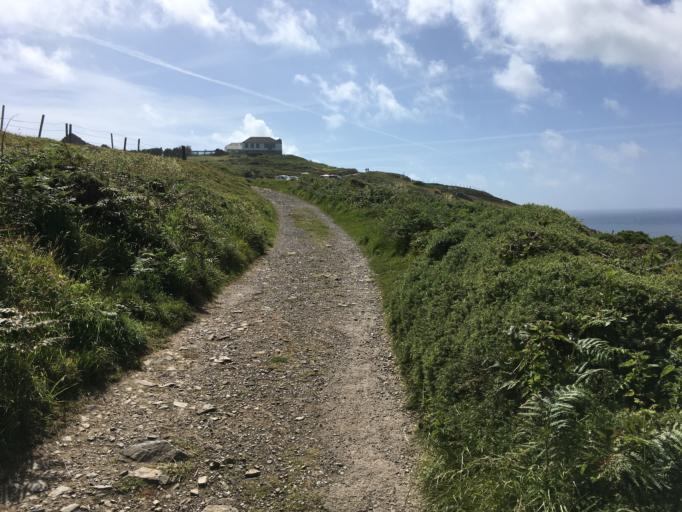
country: GB
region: England
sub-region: Cornwall
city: Saint Just
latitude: 50.1650
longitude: -5.6670
